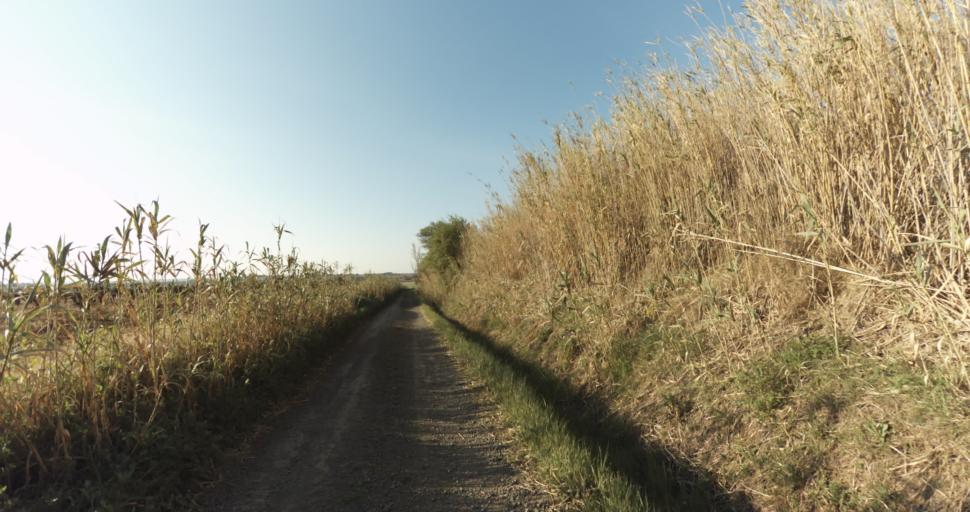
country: FR
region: Languedoc-Roussillon
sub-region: Departement de l'Herault
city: Pomerols
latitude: 43.3827
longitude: 3.5209
